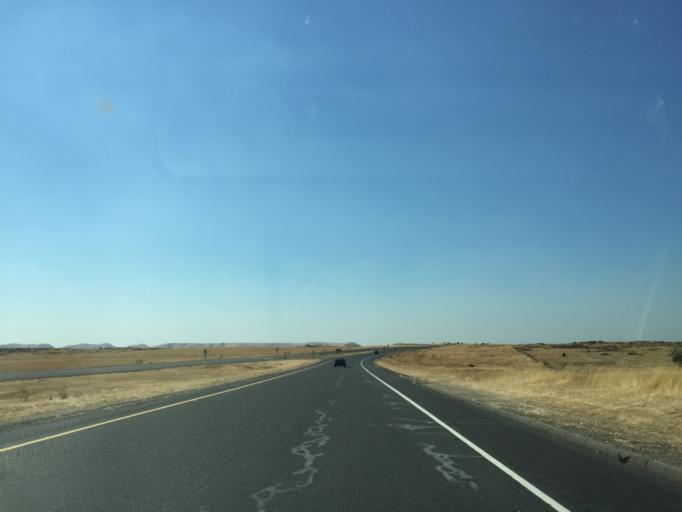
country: US
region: California
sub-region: Calaveras County
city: Copperopolis
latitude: 37.8252
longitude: -120.6383
